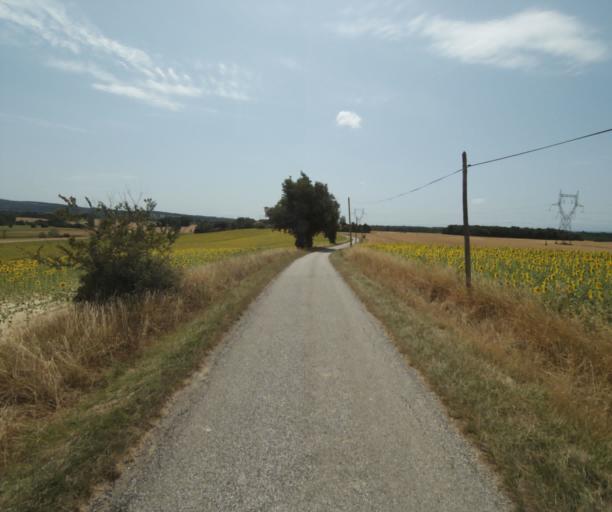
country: FR
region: Midi-Pyrenees
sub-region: Departement de la Haute-Garonne
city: Saint-Felix-Lauragais
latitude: 43.4152
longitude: 1.9119
